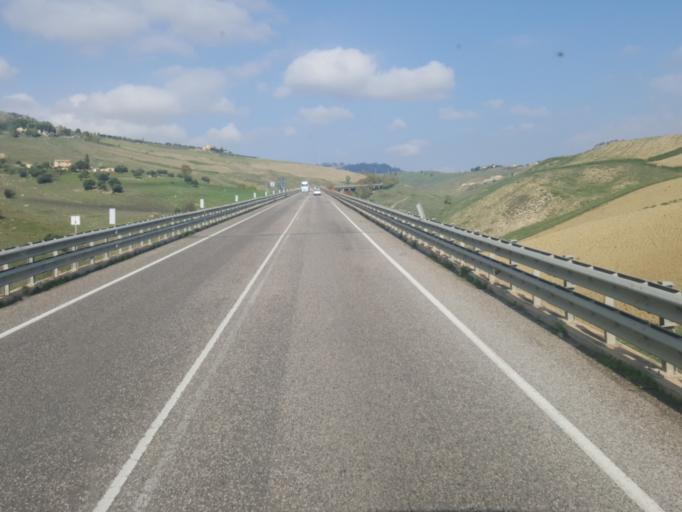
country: IT
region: Sicily
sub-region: Enna
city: Pietraperzia
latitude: 37.4603
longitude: 14.1045
